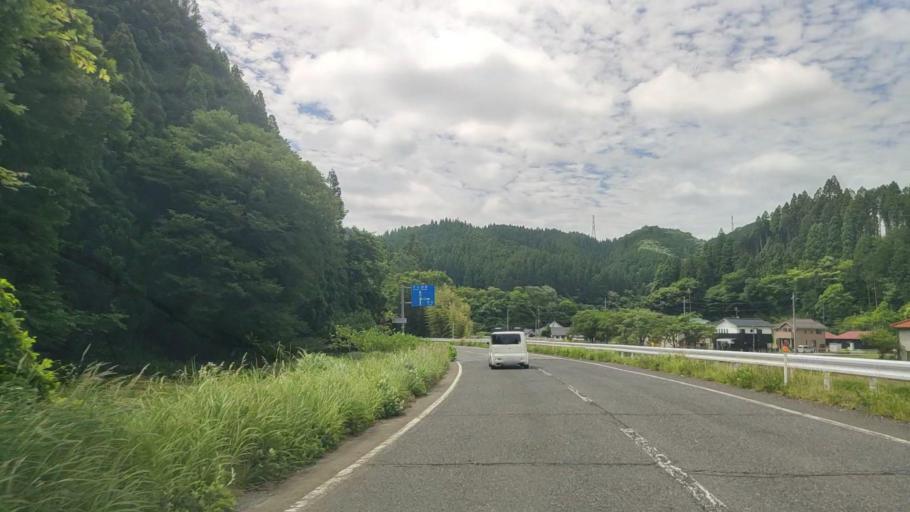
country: JP
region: Okayama
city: Niimi
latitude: 35.1743
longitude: 133.5716
